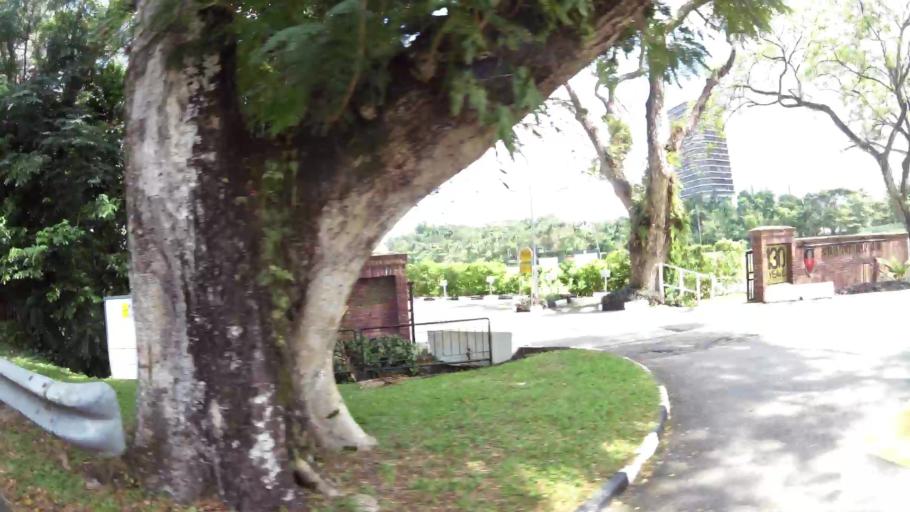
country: SG
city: Singapore
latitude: 1.3310
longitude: 103.8370
